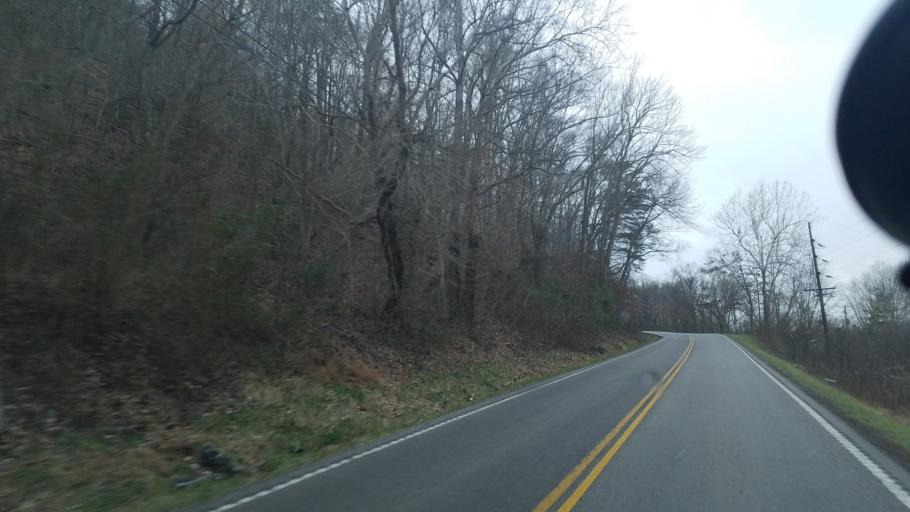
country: US
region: Ohio
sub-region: Scioto County
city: Portsmouth
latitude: 38.6892
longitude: -83.0546
